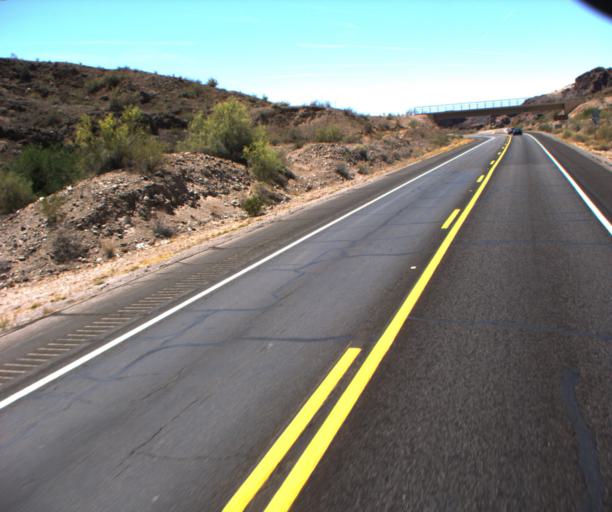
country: US
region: Arizona
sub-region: La Paz County
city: Cienega Springs
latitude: 34.2557
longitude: -114.1577
